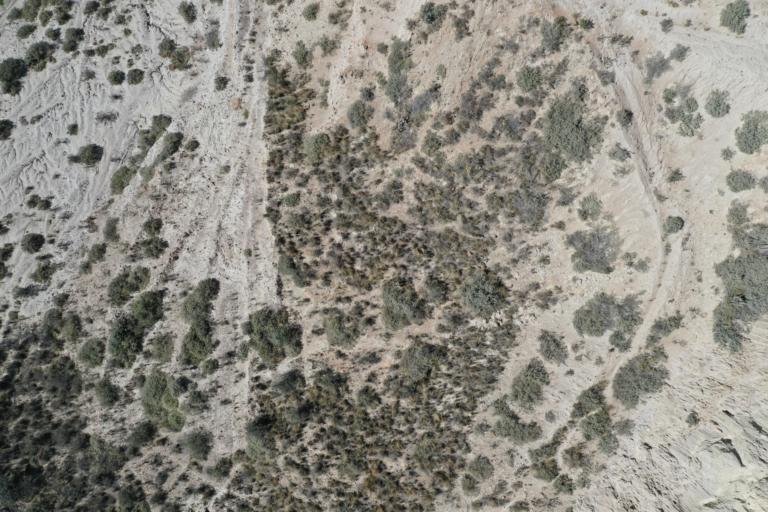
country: BO
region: La Paz
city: La Paz
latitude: -16.5516
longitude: -68.1286
